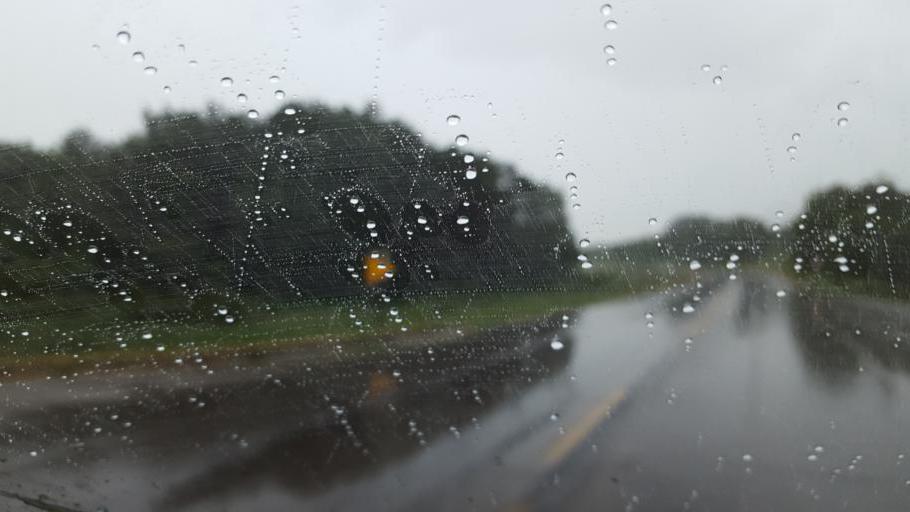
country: US
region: Wisconsin
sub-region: Vernon County
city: Hillsboro
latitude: 43.6481
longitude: -90.3523
